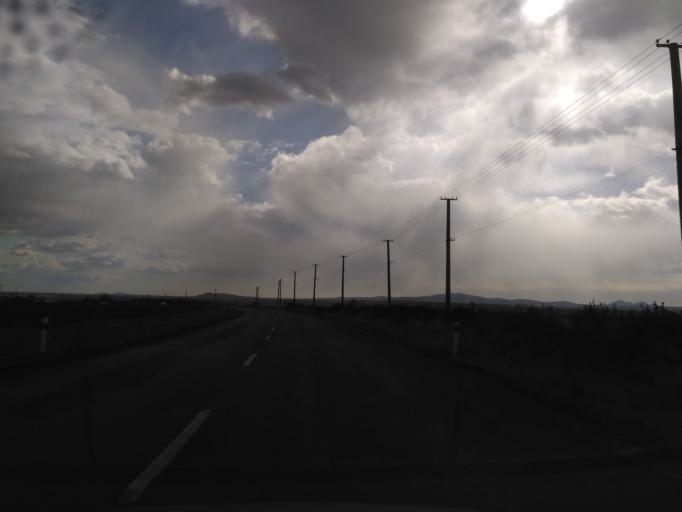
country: SK
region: Kosicky
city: Secovce
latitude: 48.6612
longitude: 21.6641
